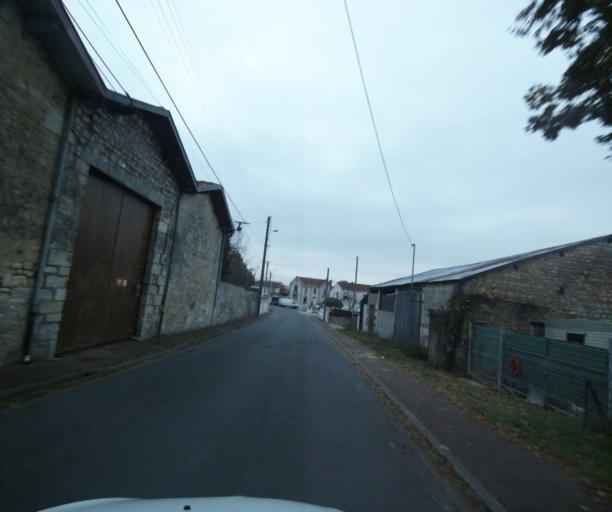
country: FR
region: Poitou-Charentes
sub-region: Departement de la Charente-Maritime
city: Saintes
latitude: 45.7405
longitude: -0.6123
